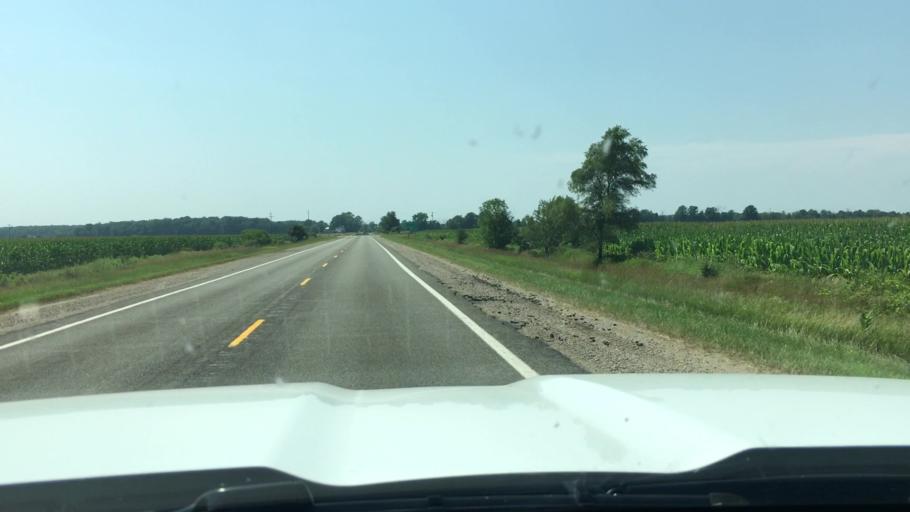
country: US
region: Michigan
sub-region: Gratiot County
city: Ithaca
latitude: 43.1758
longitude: -84.4730
